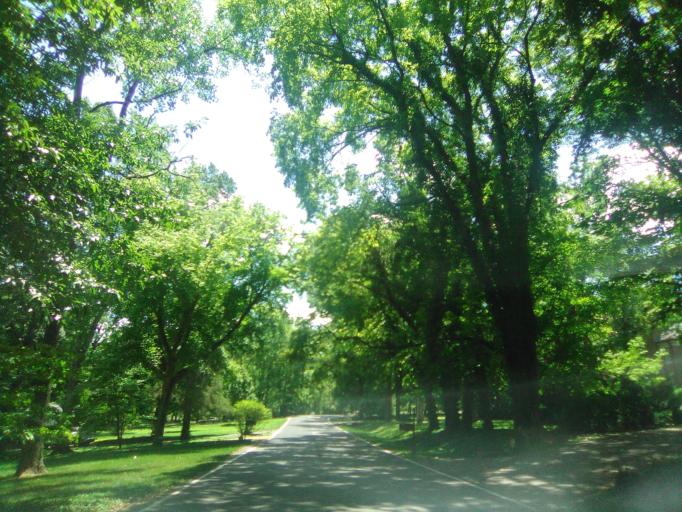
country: US
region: Tennessee
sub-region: Davidson County
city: Belle Meade
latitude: 36.1155
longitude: -86.8521
